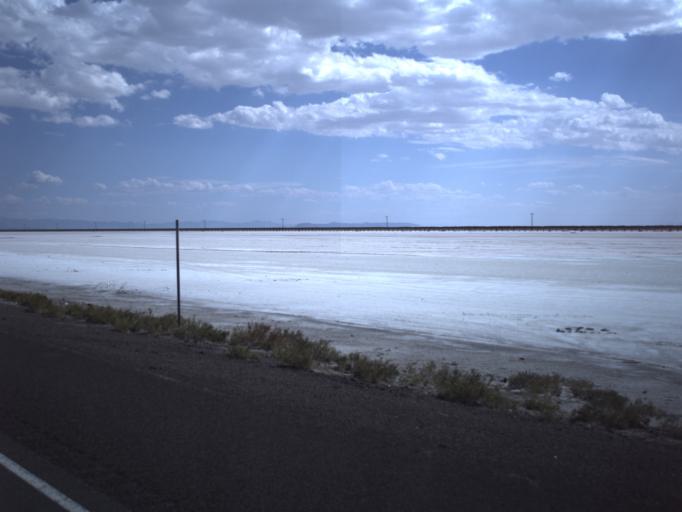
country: US
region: Utah
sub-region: Tooele County
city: Wendover
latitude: 40.7358
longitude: -113.7225
